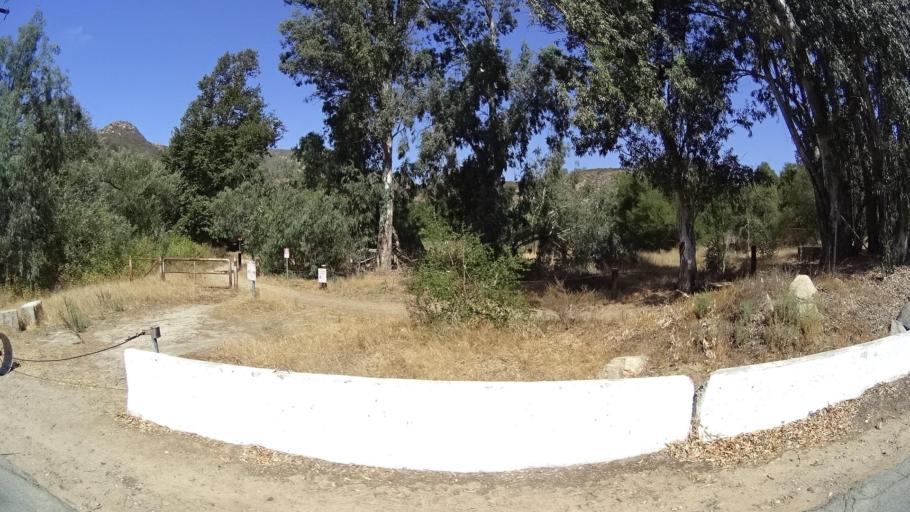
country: US
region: California
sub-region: San Diego County
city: Fallbrook
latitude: 33.4136
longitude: -117.2430
